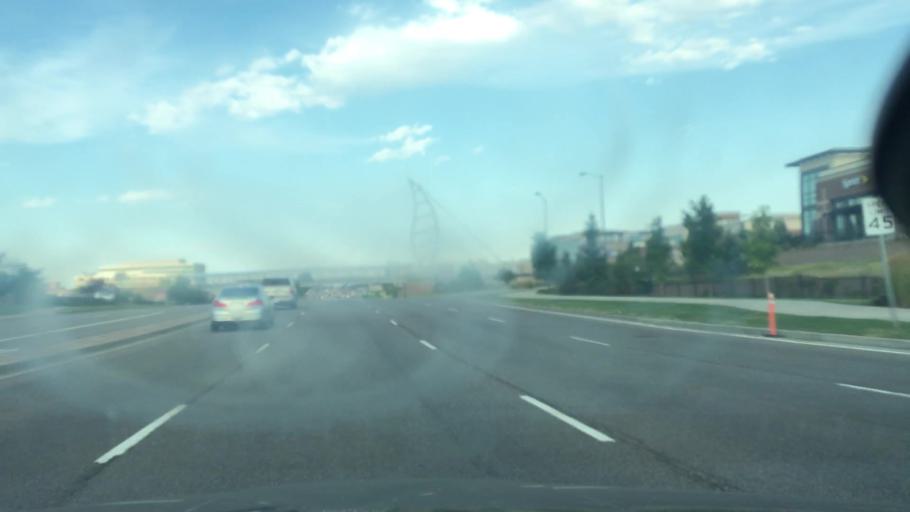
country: US
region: Colorado
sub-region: Adams County
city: Lone Tree
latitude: 39.5360
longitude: -104.8815
